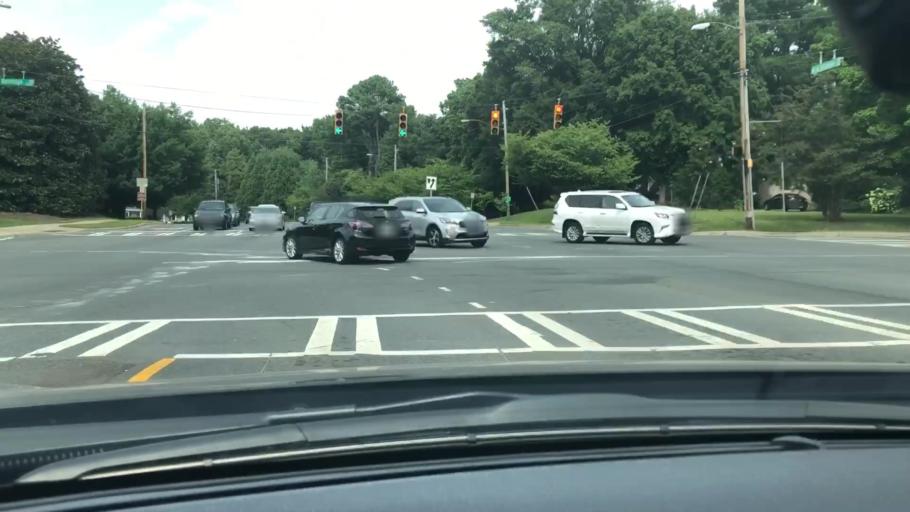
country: US
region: North Carolina
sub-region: Mecklenburg County
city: Charlotte
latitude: 35.1841
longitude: -80.8078
